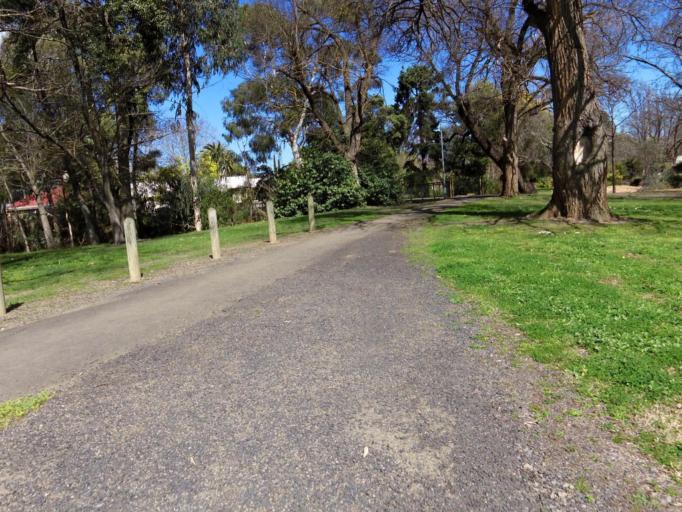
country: AU
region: Victoria
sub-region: Murrindindi
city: Alexandra
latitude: -37.1892
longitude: 145.7106
